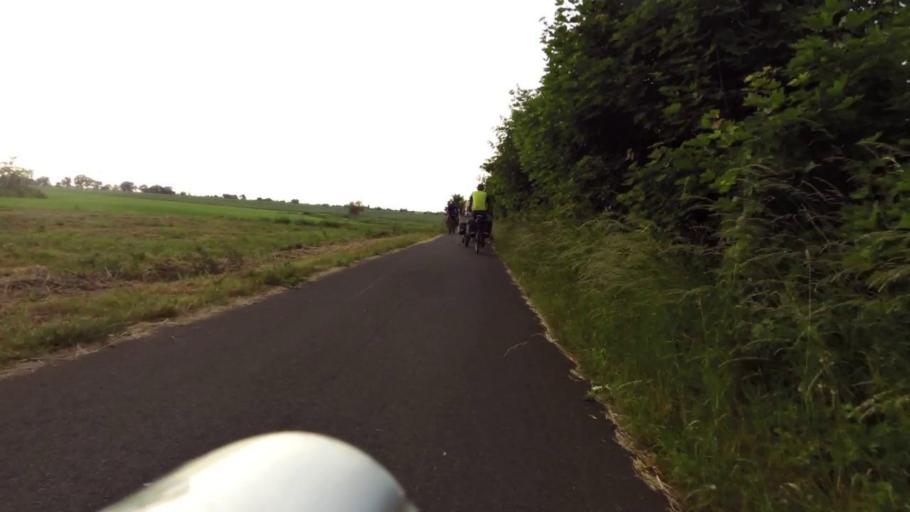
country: PL
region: Kujawsko-Pomorskie
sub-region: Powiat torunski
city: Lubianka
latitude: 53.0998
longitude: 18.5281
